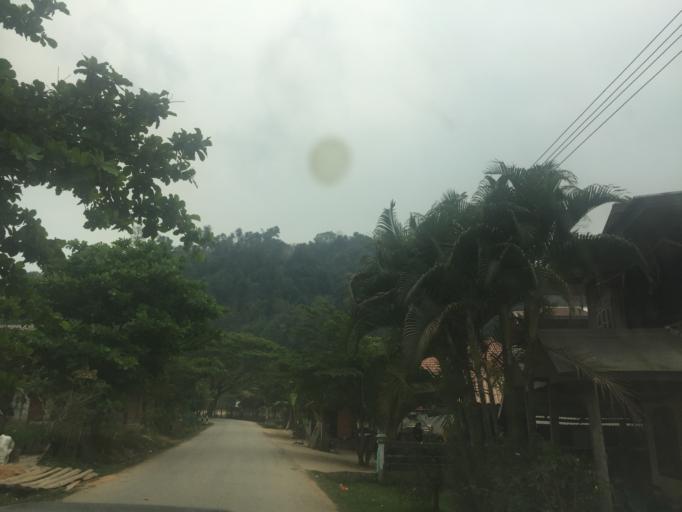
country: LA
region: Vientiane
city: Muang Sanakham
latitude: 18.3890
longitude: 101.5223
